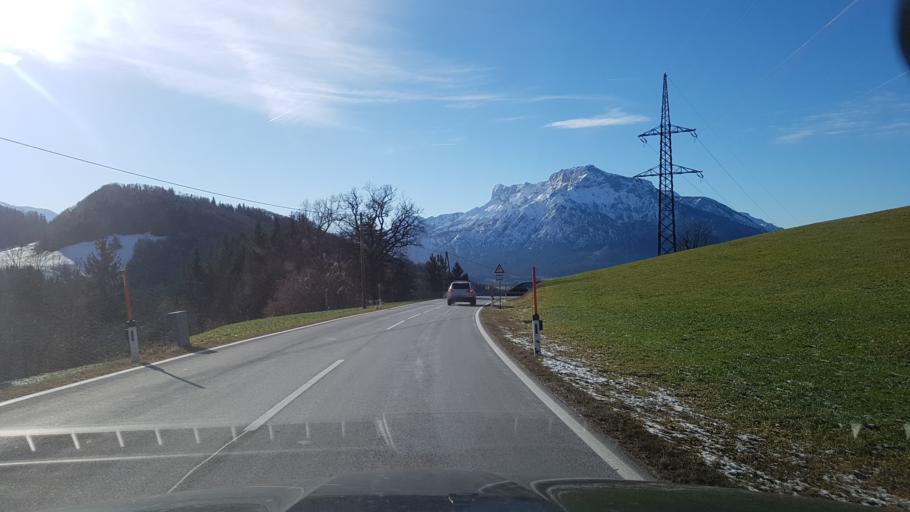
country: AT
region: Salzburg
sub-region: Politischer Bezirk Salzburg-Umgebung
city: Elsbethen
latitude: 47.7712
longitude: 13.1066
